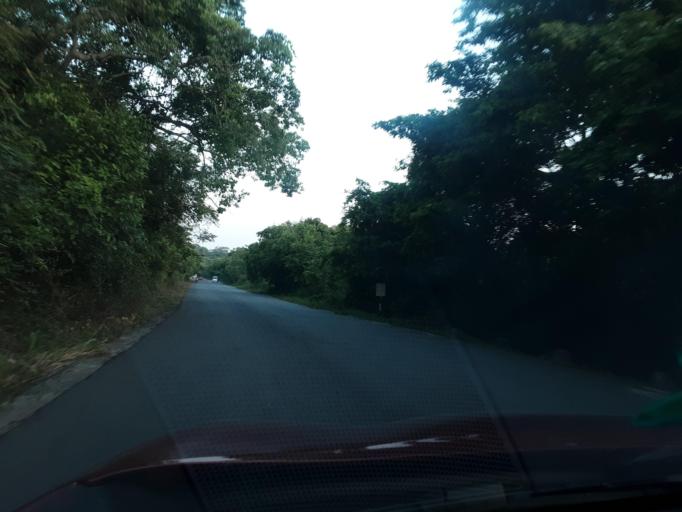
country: LK
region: Central
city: Dambulla
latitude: 7.8111
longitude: 80.7677
